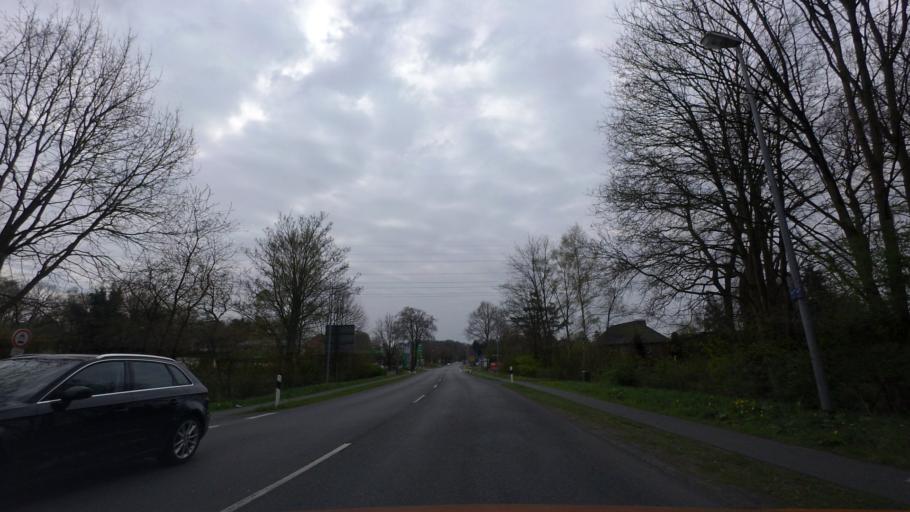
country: DE
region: Lower Saxony
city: Wildeshausen
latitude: 52.9067
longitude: 8.4419
